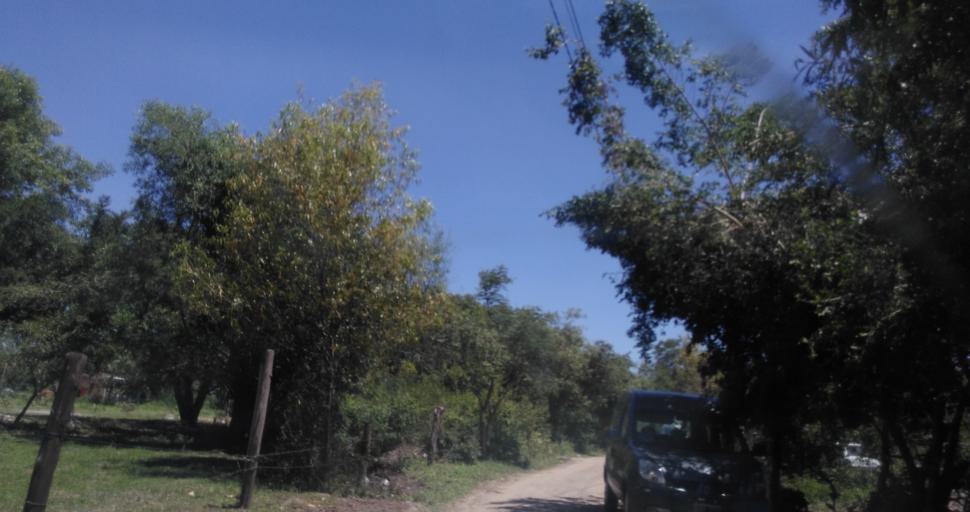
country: AR
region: Chaco
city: Fontana
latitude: -27.4159
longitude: -59.0102
